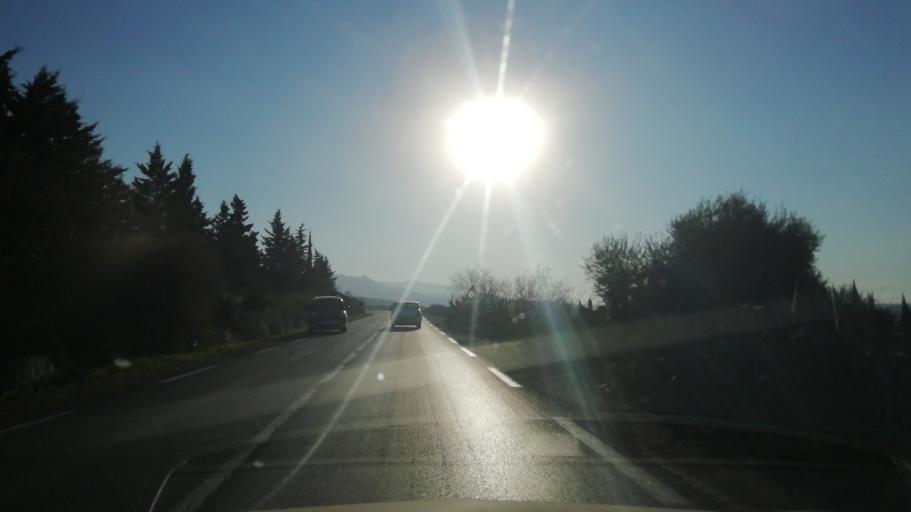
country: DZ
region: Tlemcen
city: Beni Mester
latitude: 34.8595
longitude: -1.4494
